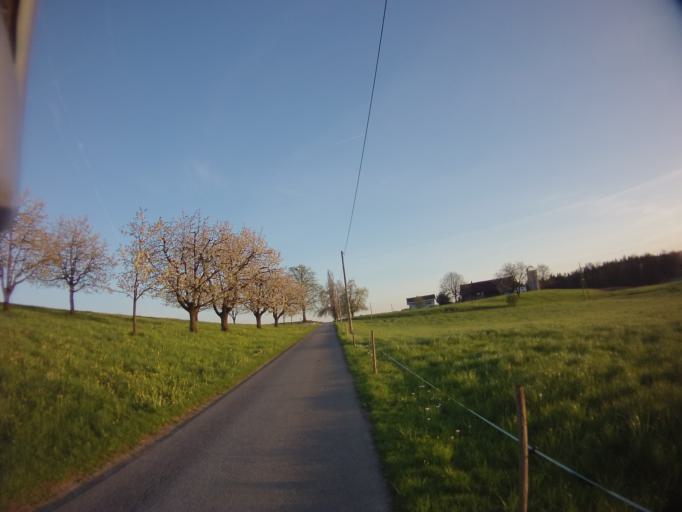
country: CH
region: Zurich
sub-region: Bezirk Affoltern
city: Knonau
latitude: 47.2104
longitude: 8.4500
